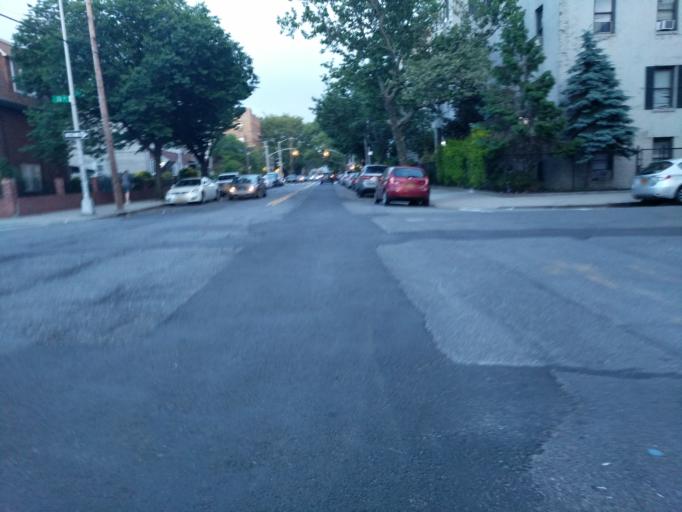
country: US
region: New York
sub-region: Queens County
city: Long Island City
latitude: 40.7773
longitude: -73.9075
